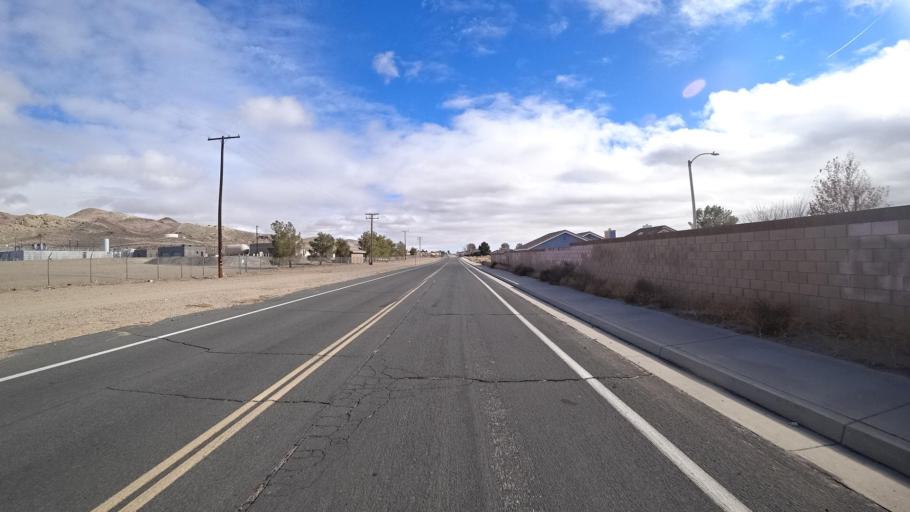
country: US
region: California
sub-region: Kern County
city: Rosamond
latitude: 34.8711
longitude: -118.1919
